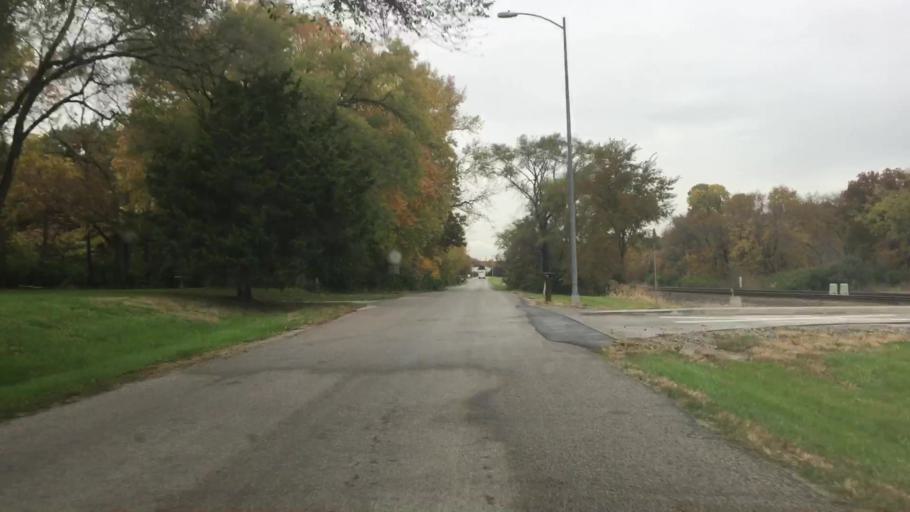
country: US
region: Kansas
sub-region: Wyandotte County
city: Edwardsville
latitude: 38.9957
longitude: -94.8223
